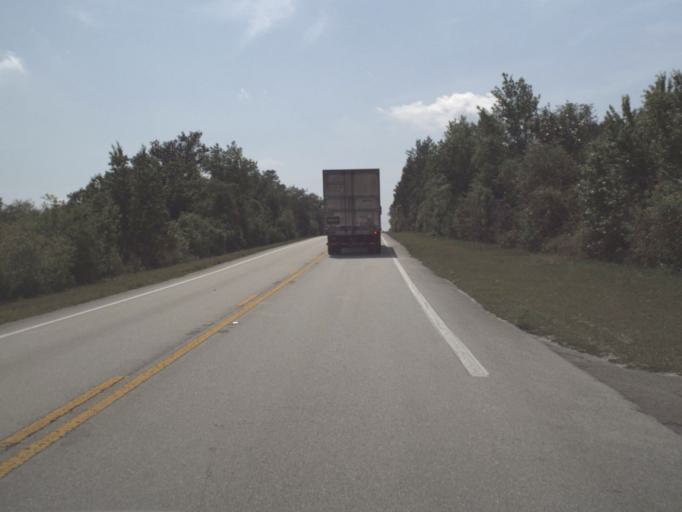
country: US
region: Florida
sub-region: Lake County
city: Astor
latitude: 29.2808
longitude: -81.6495
